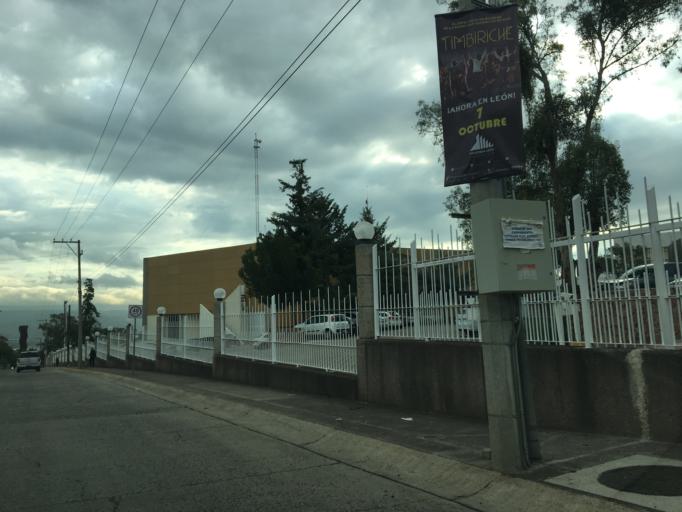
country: MX
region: Guanajuato
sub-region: Leon
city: La Ermita
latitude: 21.1664
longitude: -101.7174
